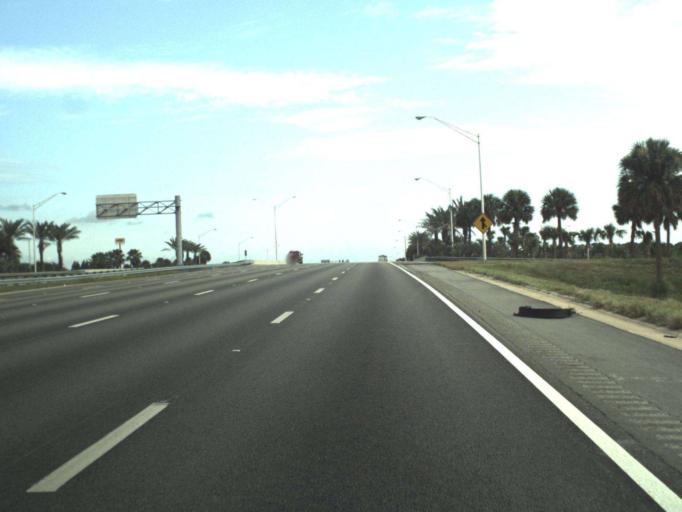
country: US
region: Florida
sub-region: Saint Lucie County
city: Fort Pierce South
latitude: 27.4141
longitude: -80.3882
